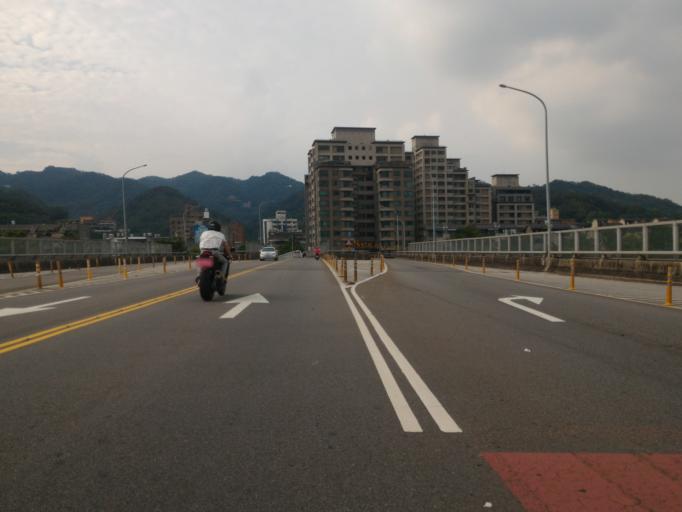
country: TW
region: Taiwan
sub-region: Taoyuan
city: Taoyuan
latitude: 24.9672
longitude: 121.3941
